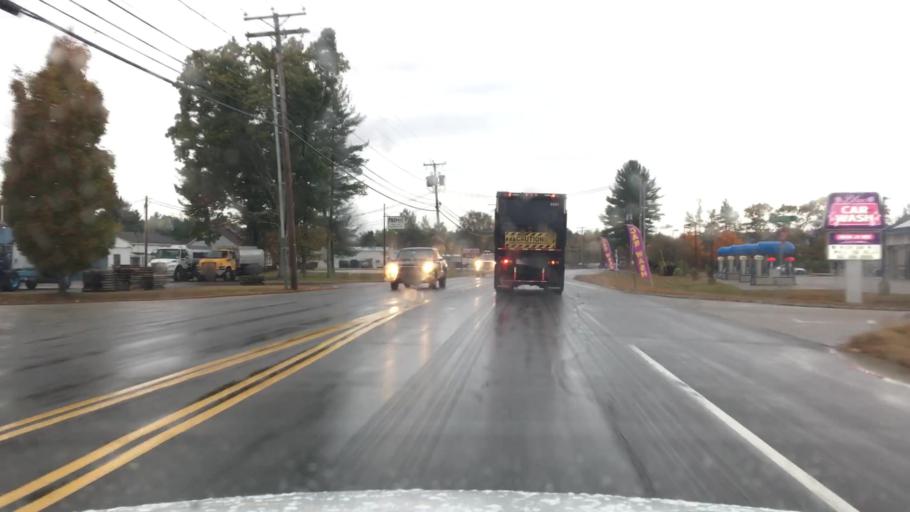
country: US
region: New Hampshire
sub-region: Strafford County
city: Somersworth
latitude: 43.2586
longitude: -70.9029
